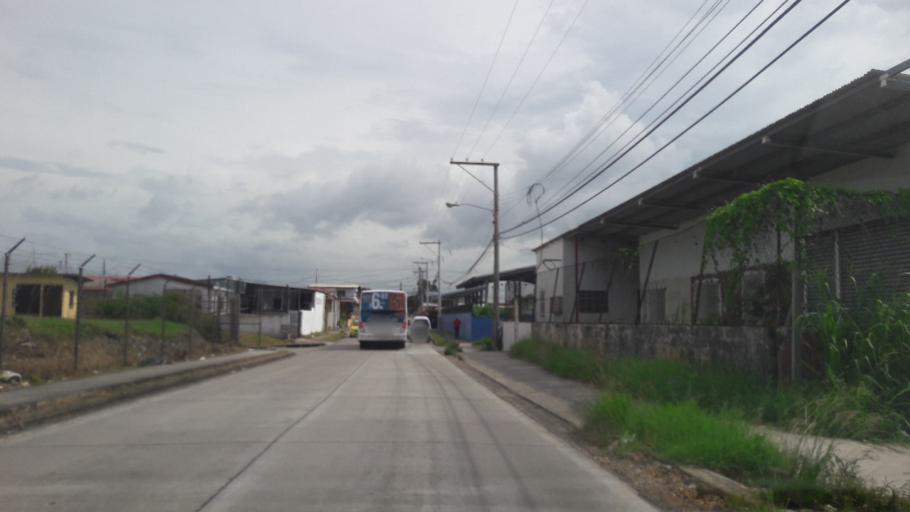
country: PA
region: Panama
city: Tocumen
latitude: 9.0504
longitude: -79.4156
